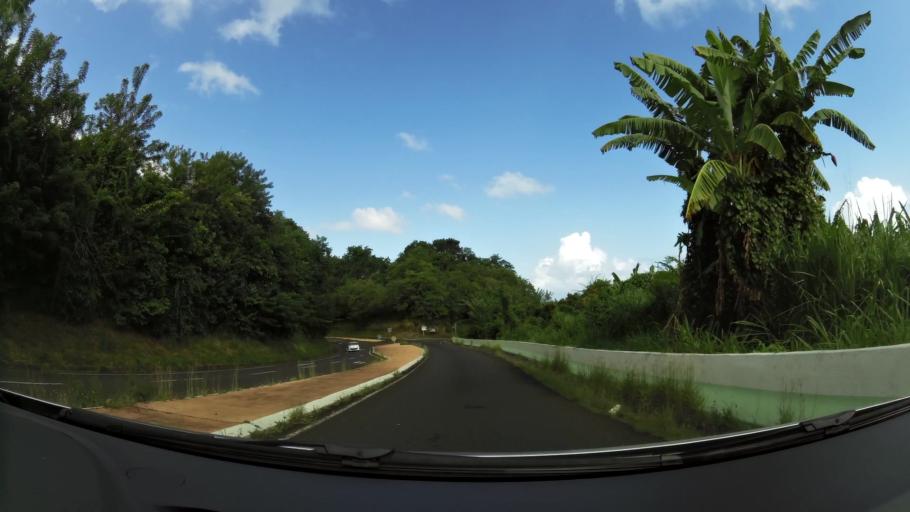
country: MQ
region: Martinique
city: Petite Riviere Salee
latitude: 14.7520
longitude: -60.9744
